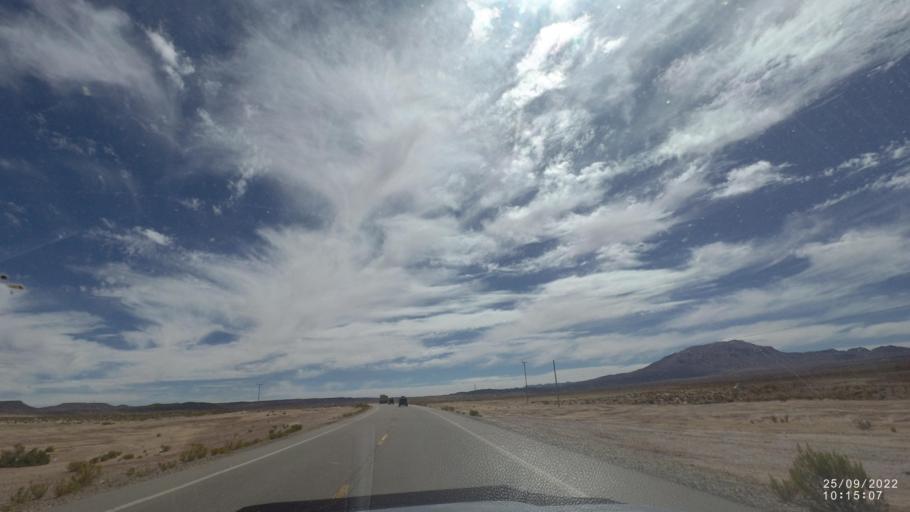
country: BO
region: Potosi
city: Colchani
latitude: -20.0531
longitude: -66.8715
